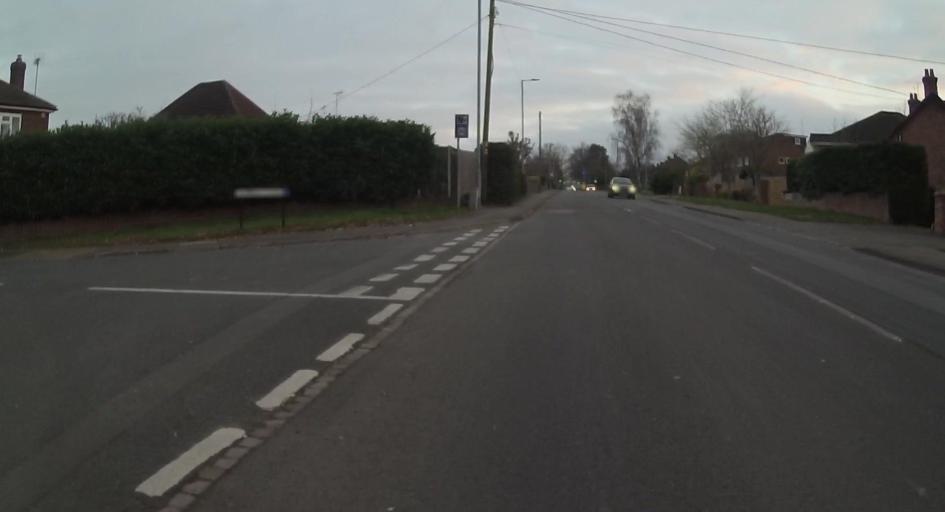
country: GB
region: England
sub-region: Bracknell Forest
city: Bracknell
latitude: 51.4250
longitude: -0.7637
